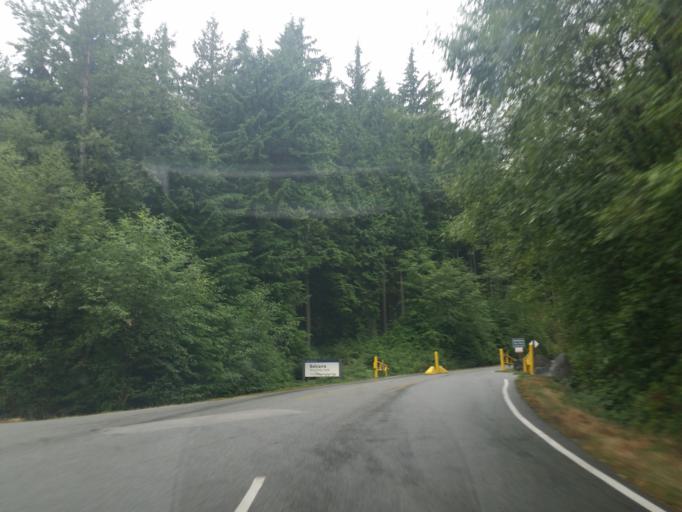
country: CA
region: British Columbia
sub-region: Greater Vancouver Regional District
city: Anmore
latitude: 49.3114
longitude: -122.8932
